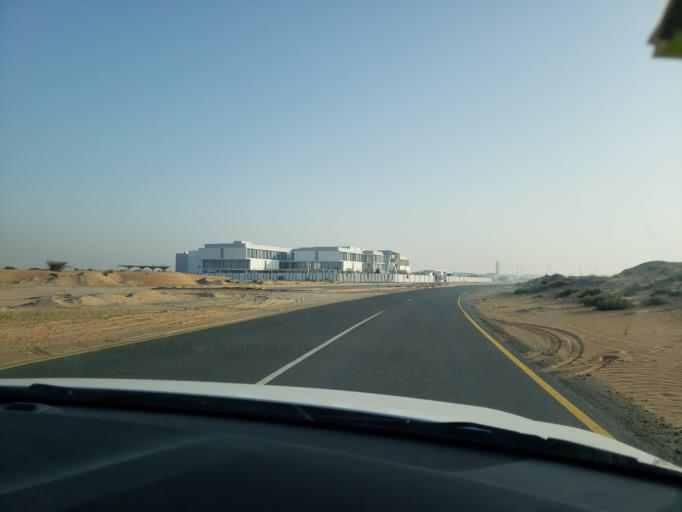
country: AE
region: Umm al Qaywayn
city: Umm al Qaywayn
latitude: 25.4656
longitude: 55.6111
